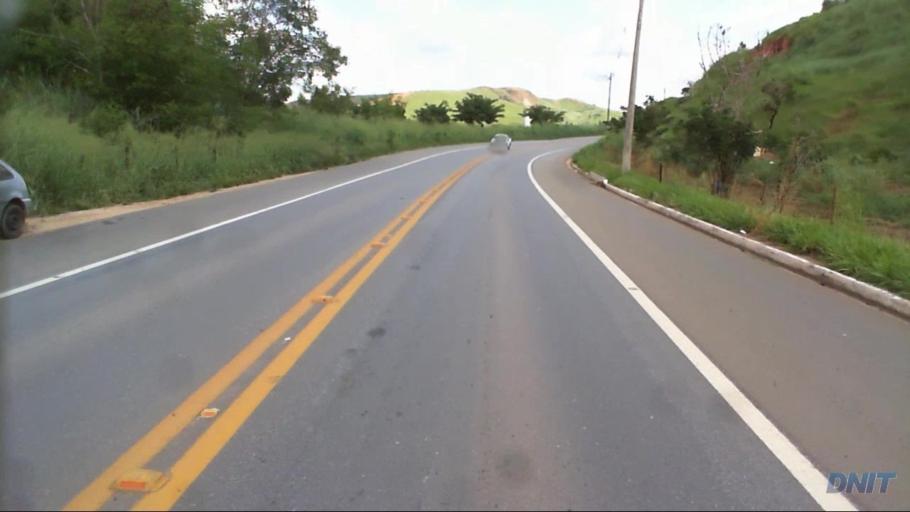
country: BR
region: Minas Gerais
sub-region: Governador Valadares
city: Governador Valadares
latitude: -18.8453
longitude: -41.9753
